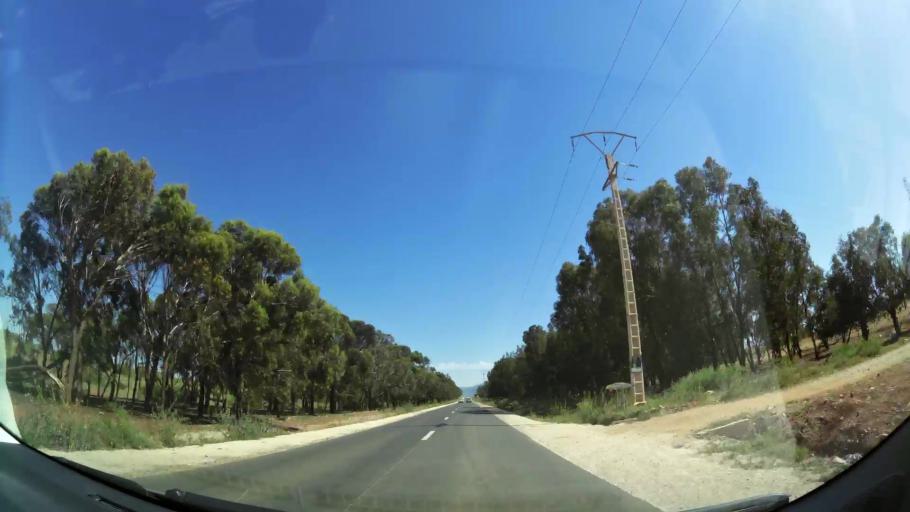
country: MA
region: Oriental
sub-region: Berkane-Taourirt
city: Madagh
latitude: 35.0023
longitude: -2.3963
